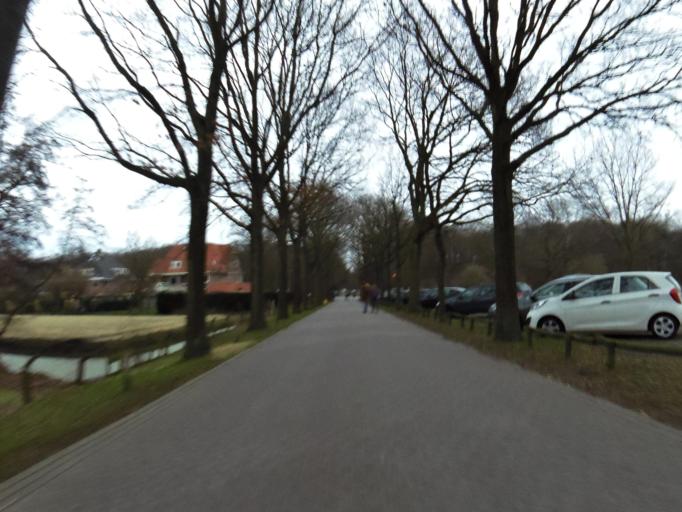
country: NL
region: North Holland
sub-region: Gemeente Bloemendaal
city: Bennebroek
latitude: 52.3457
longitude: 4.5834
